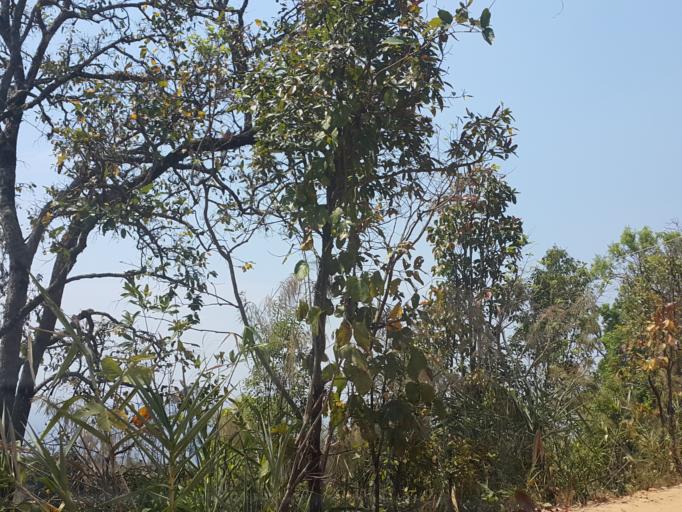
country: TH
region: Chiang Mai
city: Samoeng
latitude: 18.8904
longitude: 98.7763
